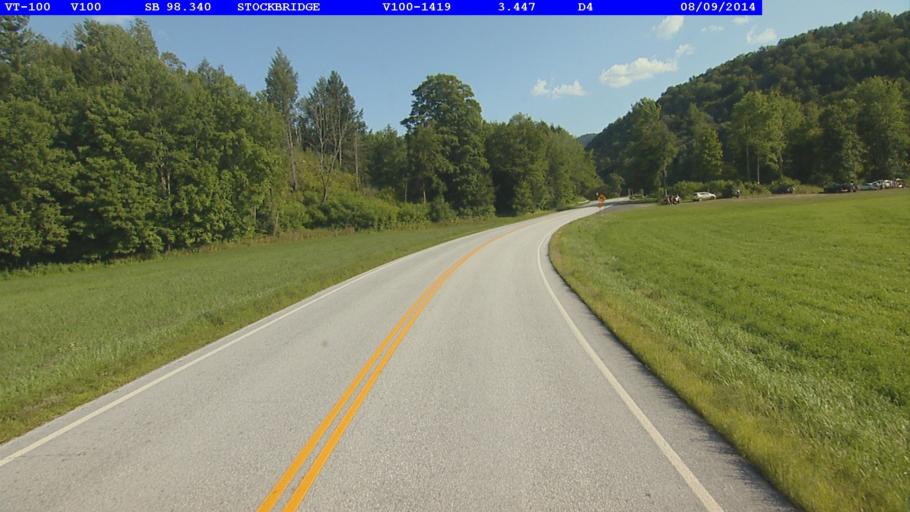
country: US
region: Vermont
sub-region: Orange County
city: Randolph
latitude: 43.7886
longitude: -72.7603
